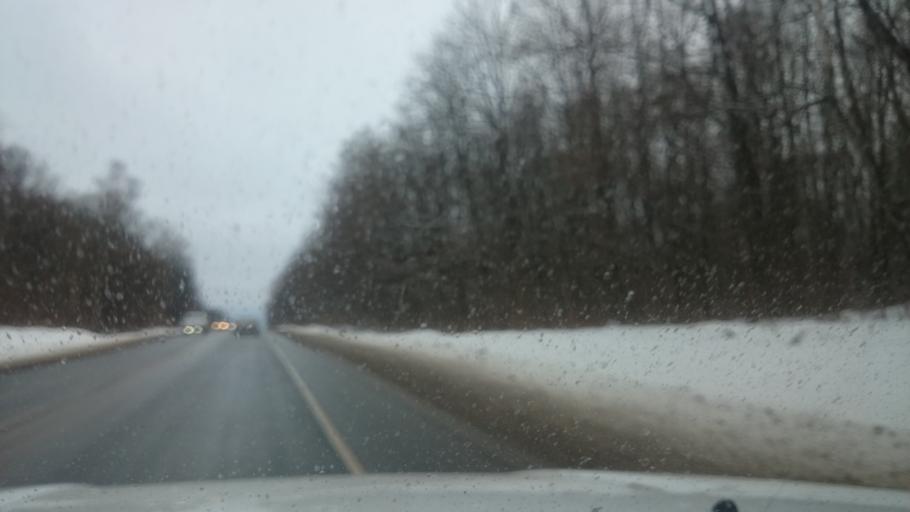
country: RU
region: Tula
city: Kosaya Gora
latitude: 54.0917
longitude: 37.5476
